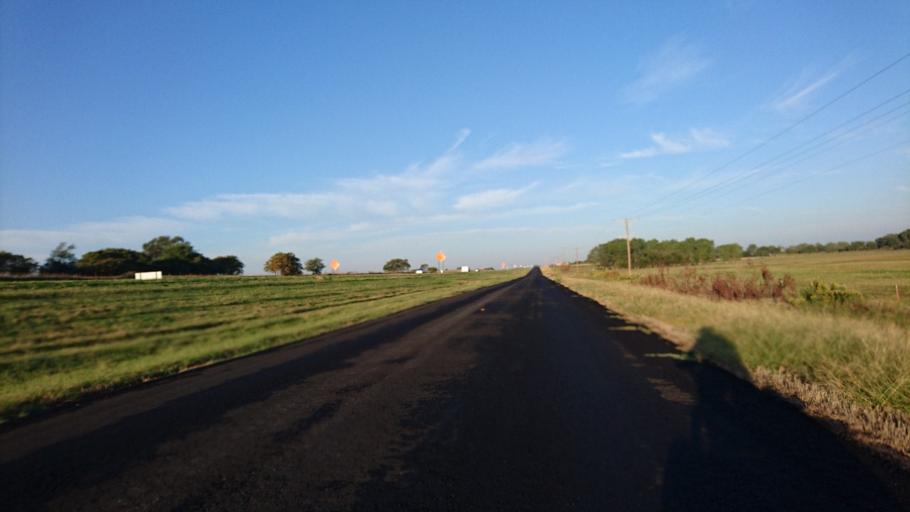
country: US
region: Oklahoma
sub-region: Beckham County
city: Sayre
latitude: 35.2625
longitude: -99.6892
